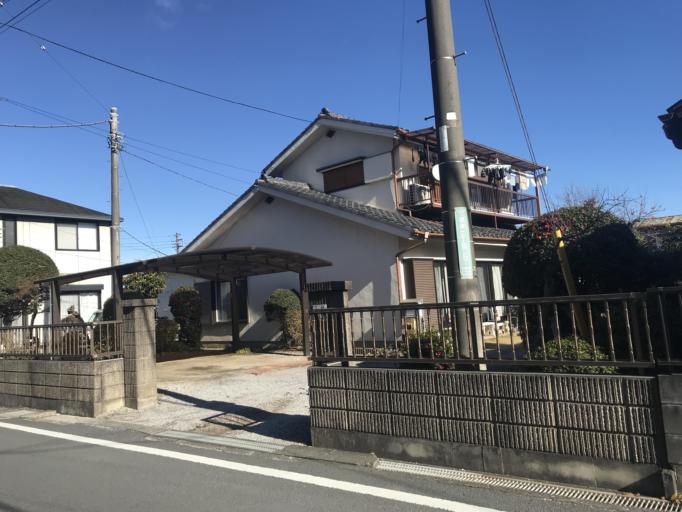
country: JP
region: Saitama
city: Sayama
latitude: 35.8561
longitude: 139.3822
